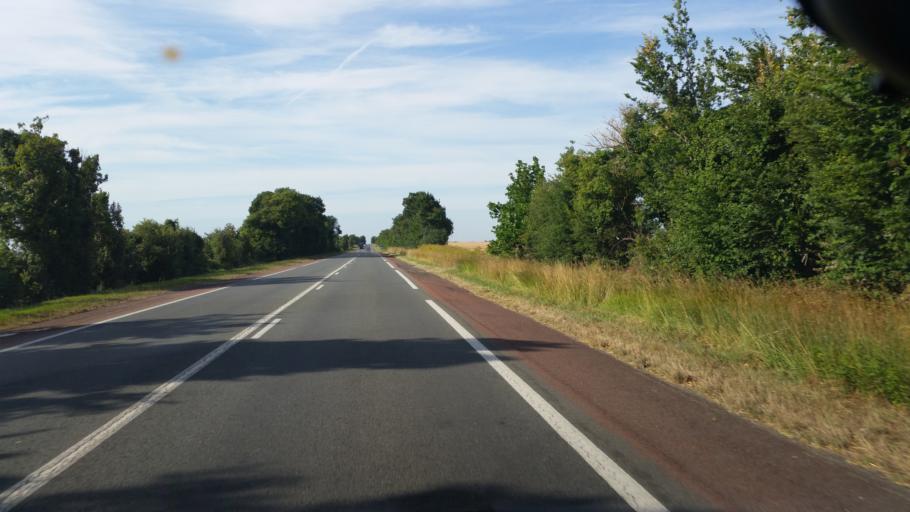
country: FR
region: Poitou-Charentes
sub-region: Departement de la Charente-Maritime
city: Andilly
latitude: 46.2463
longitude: -1.0149
